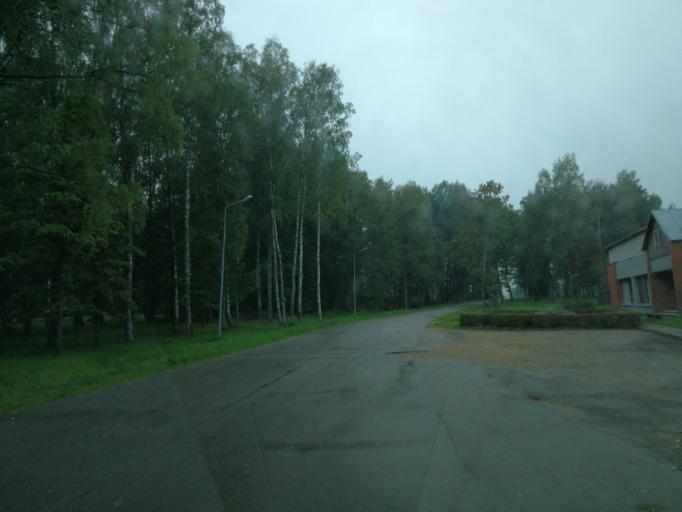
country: LV
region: Preilu Rajons
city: Jaunaglona
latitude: 56.3618
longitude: 27.0053
